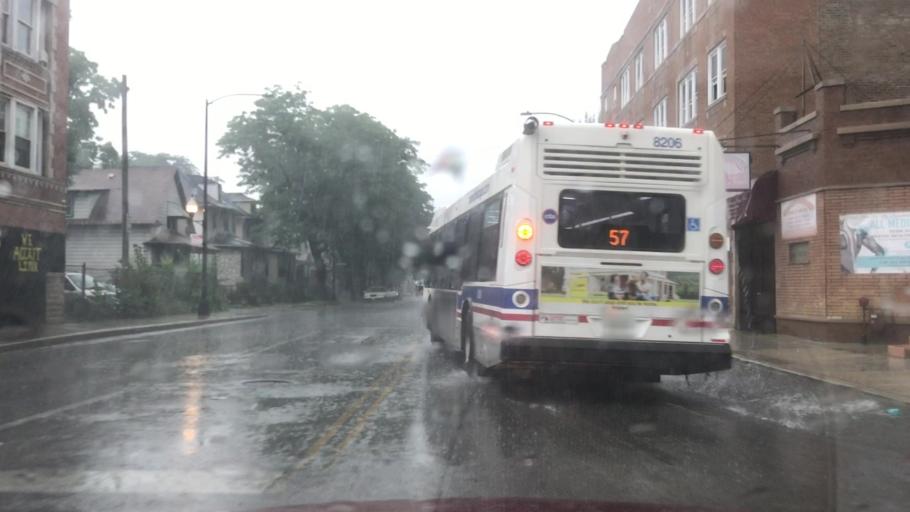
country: US
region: Illinois
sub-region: Cook County
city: Oak Park
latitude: 41.8824
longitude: -87.7551
